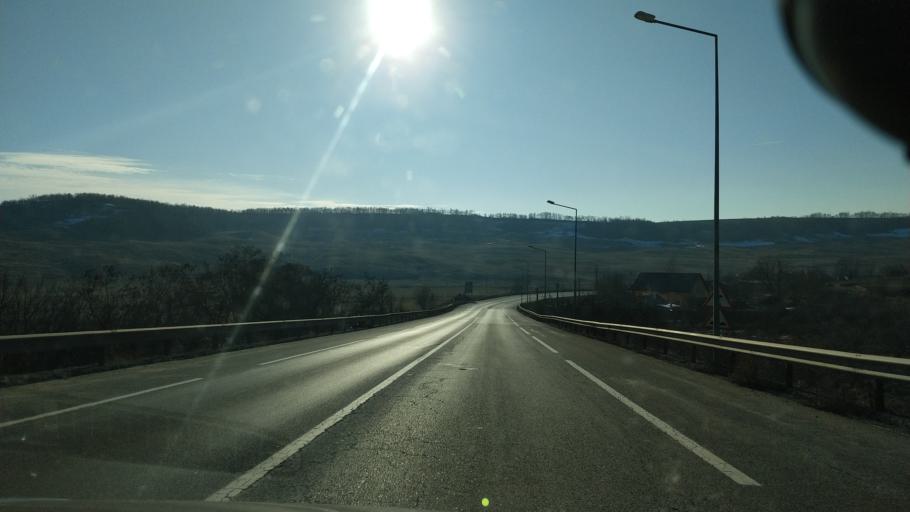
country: RO
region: Iasi
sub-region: Comuna Targu Frumos
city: Targu Frumos
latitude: 47.1976
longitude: 26.9986
